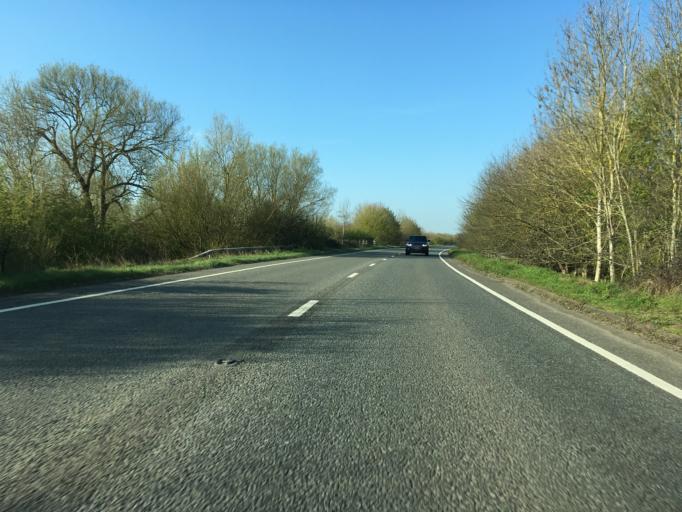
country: GB
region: England
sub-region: Northamptonshire
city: Deanshanger
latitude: 52.0487
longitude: -0.8756
